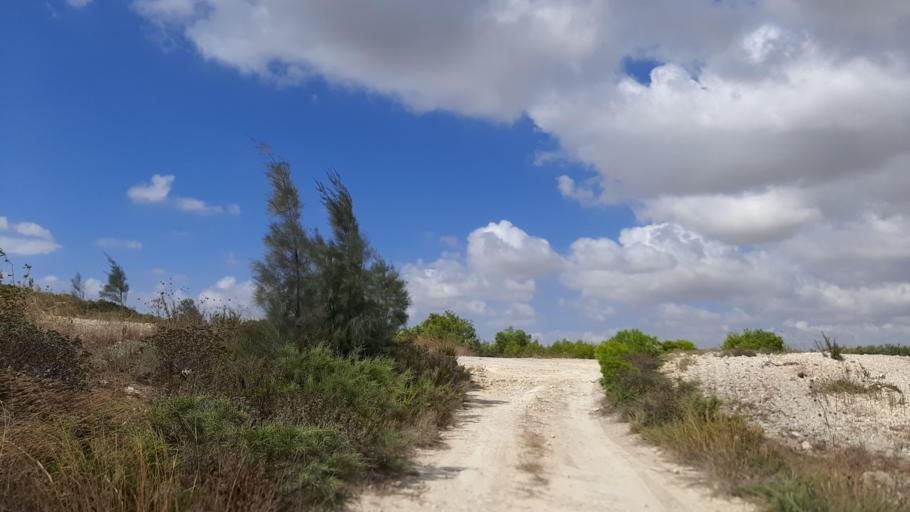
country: TN
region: Zaghwan
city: Zaghouan
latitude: 36.4974
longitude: 10.1724
